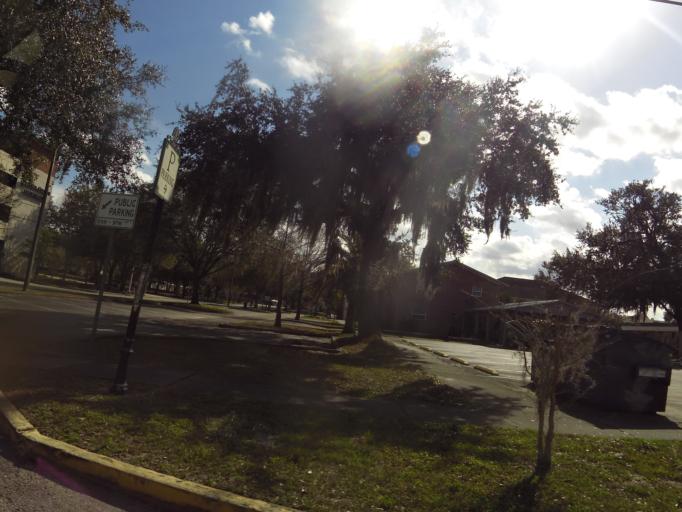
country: US
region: Florida
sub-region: Volusia County
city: DeLand
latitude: 29.0299
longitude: -81.3016
